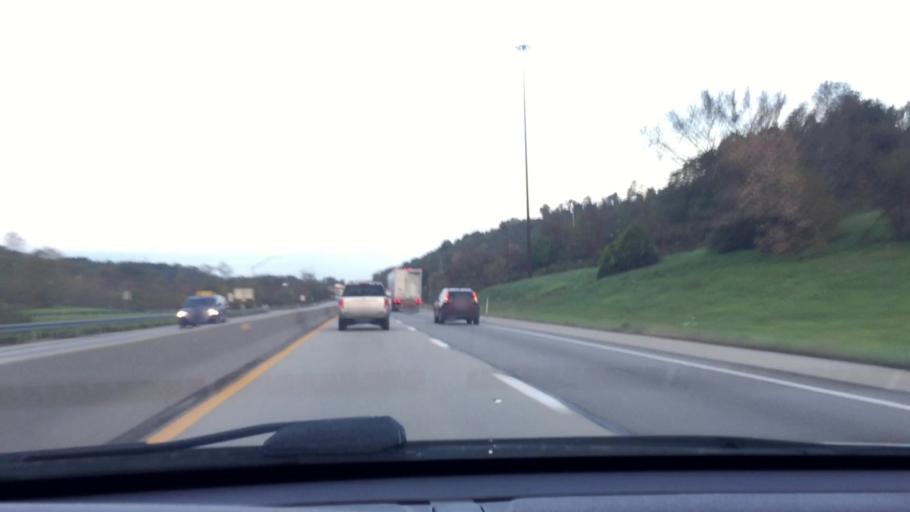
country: US
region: Pennsylvania
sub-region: Washington County
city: Charleroi
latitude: 40.1103
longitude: -79.9237
